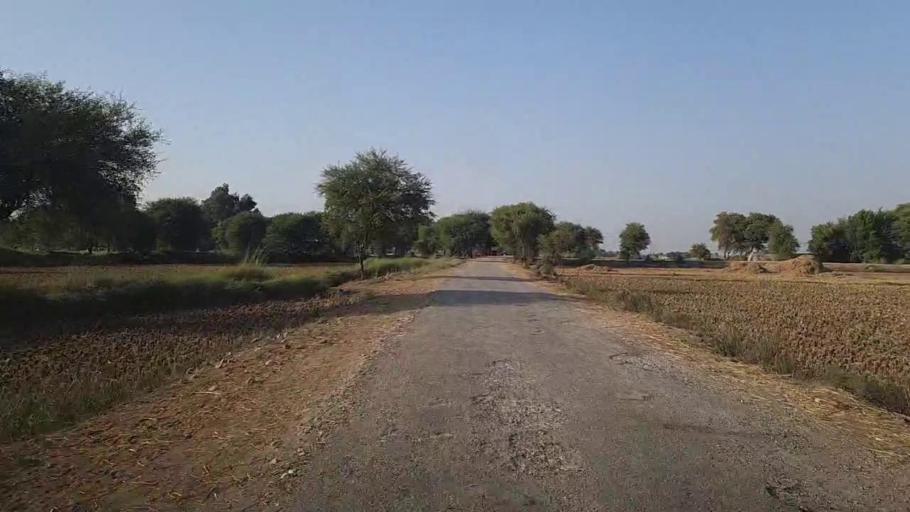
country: PK
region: Sindh
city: Kashmor
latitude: 28.4217
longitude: 69.4080
